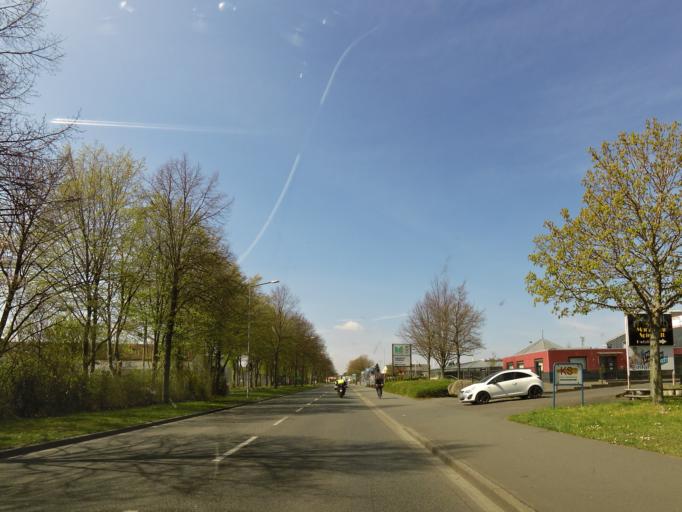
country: DE
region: Lower Saxony
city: Wunstorf
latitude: 52.4294
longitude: 9.4224
